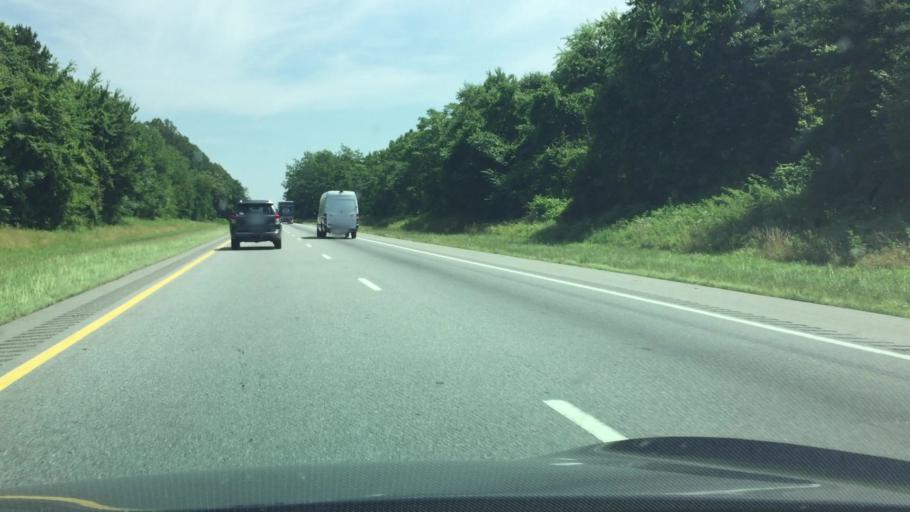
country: US
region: North Carolina
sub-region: Yadkin County
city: Jonesville
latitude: 36.0773
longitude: -80.8198
